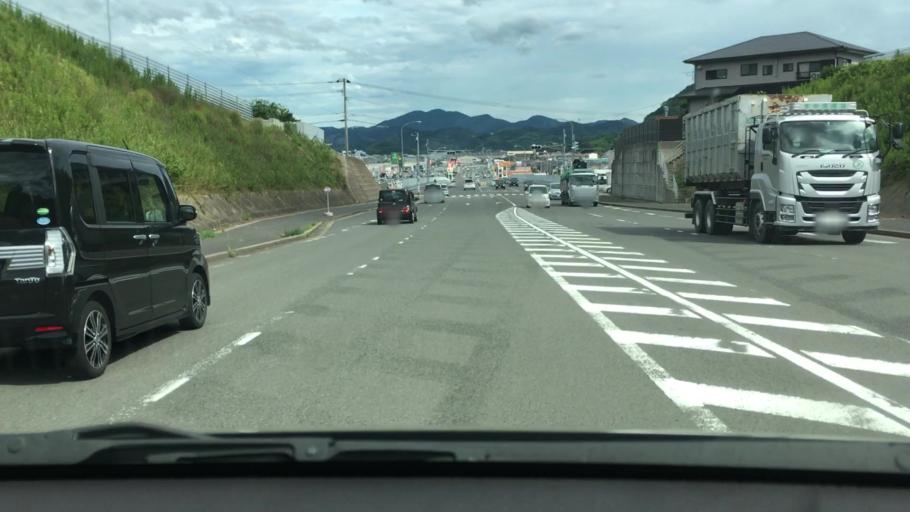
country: JP
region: Nagasaki
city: Togitsu
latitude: 32.8555
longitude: 129.8213
